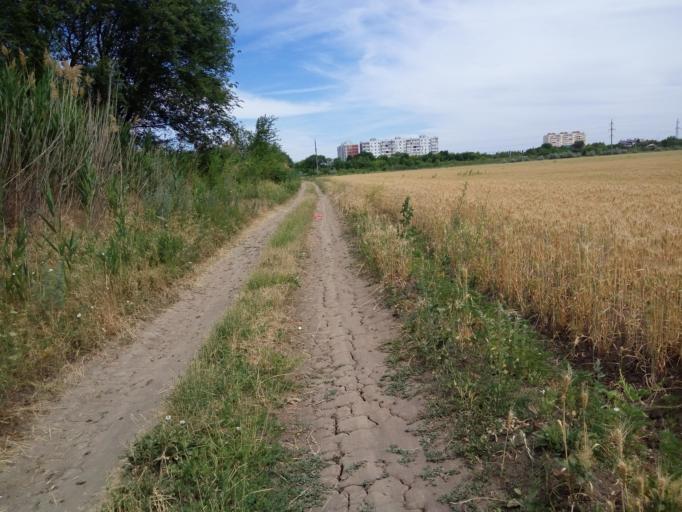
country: RU
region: Rostov
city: Bataysk
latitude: 47.1212
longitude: 39.7265
